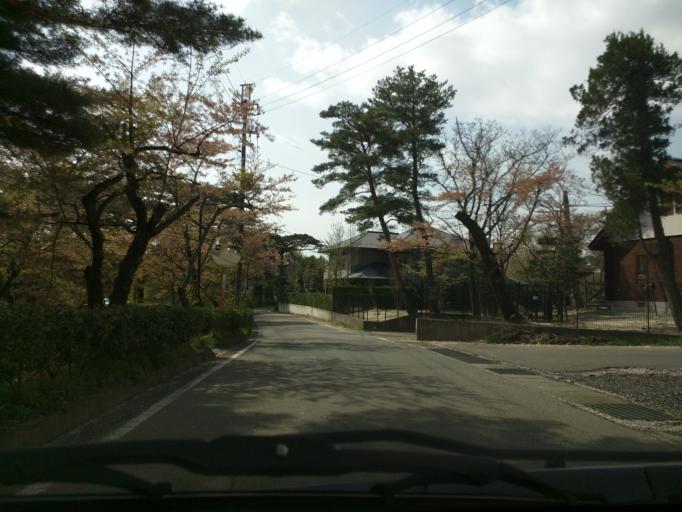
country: JP
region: Fukushima
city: Nihommatsu
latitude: 37.6042
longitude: 140.3593
